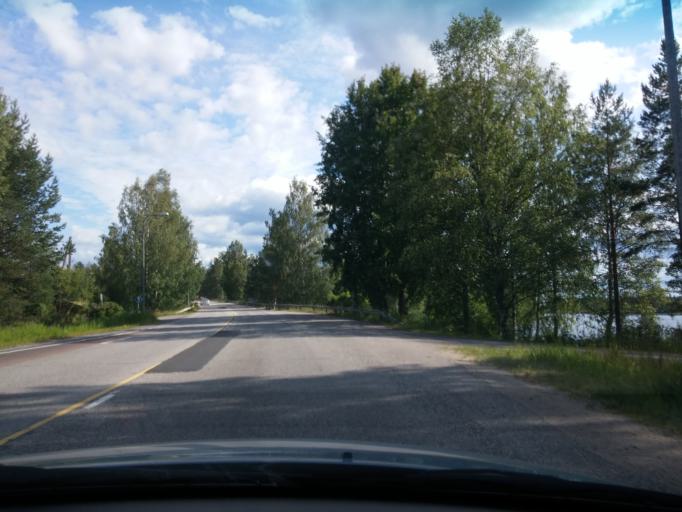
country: FI
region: Central Finland
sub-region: Keuruu
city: Keuruu
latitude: 62.2704
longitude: 24.6898
